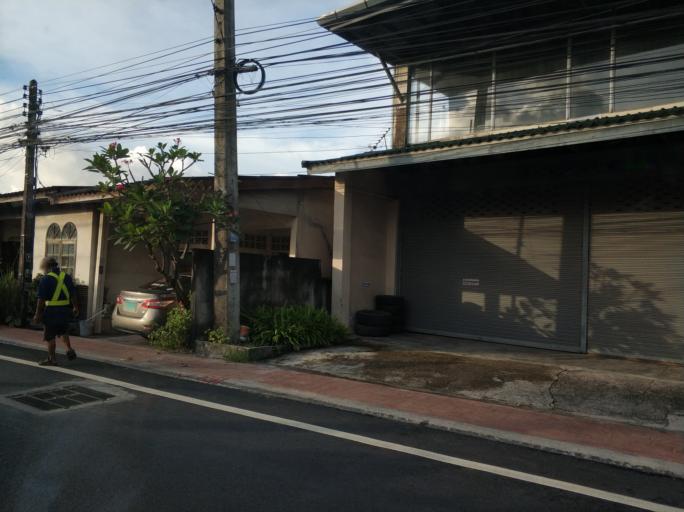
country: TH
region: Phuket
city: Kathu
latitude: 7.8995
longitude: 98.3429
